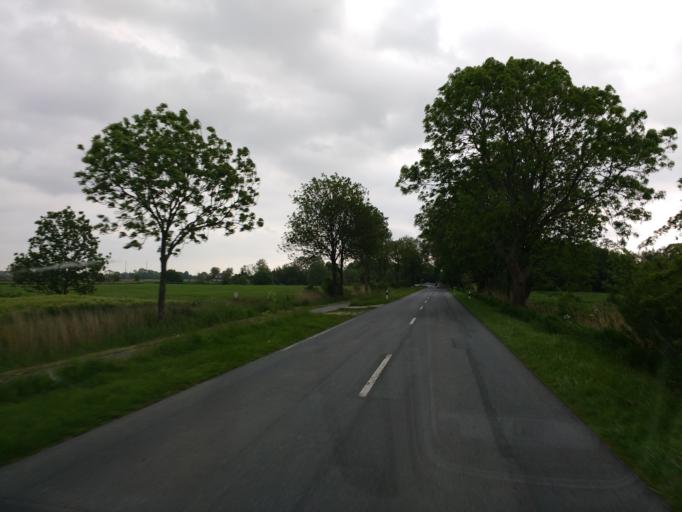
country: DE
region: Lower Saxony
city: Schillig
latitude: 53.6419
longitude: 8.0030
